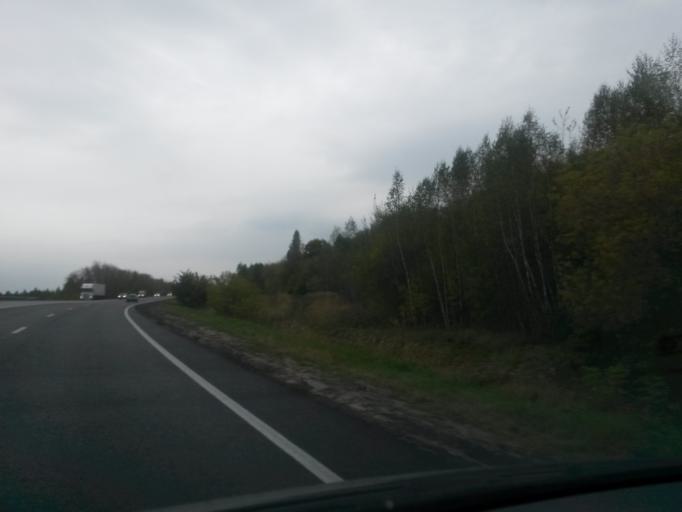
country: RU
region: Nizjnij Novgorod
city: Pamyat' Parizhskoy Kommuny
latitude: 56.0248
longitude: 44.6249
